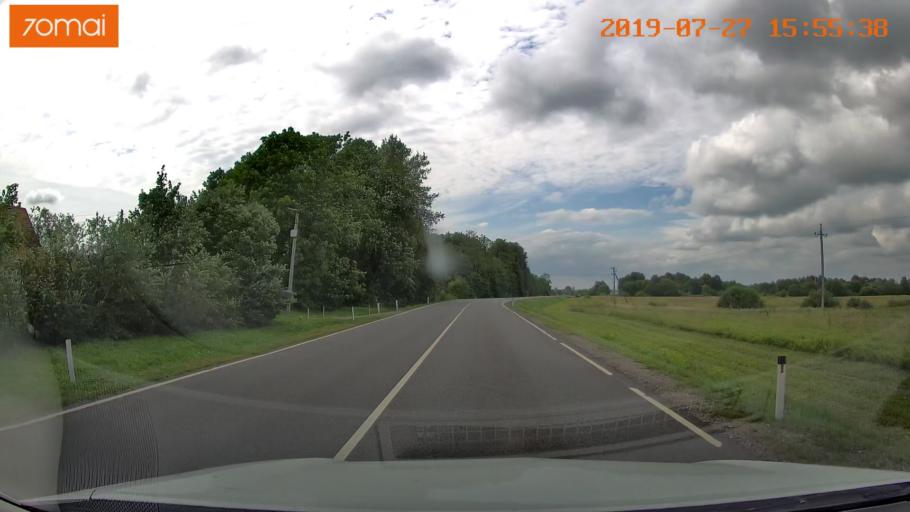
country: RU
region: Kaliningrad
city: Chernyakhovsk
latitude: 54.6143
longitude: 21.9168
